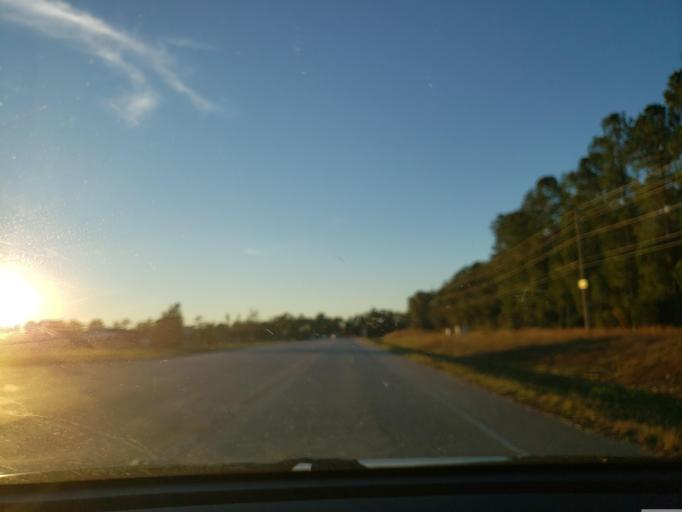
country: US
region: North Carolina
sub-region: Onslow County
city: Sneads Ferry
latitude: 34.5888
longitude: -77.4757
